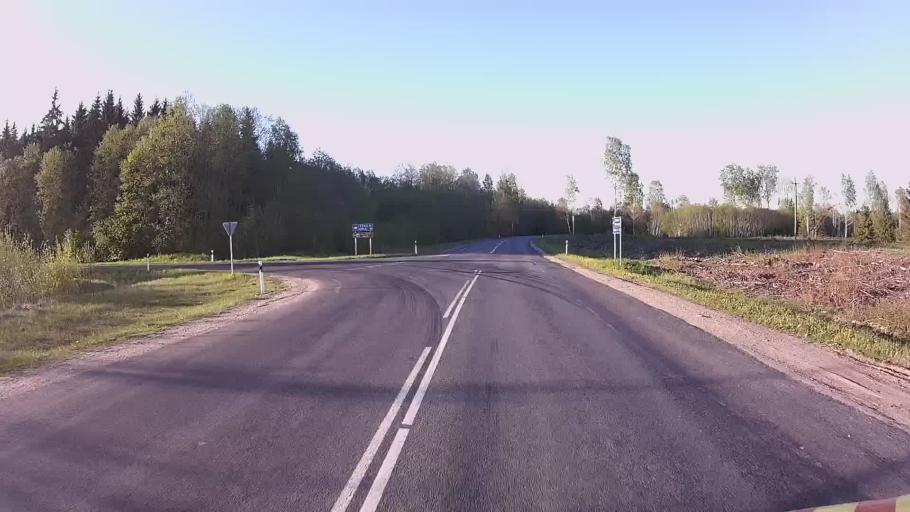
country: EE
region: Viljandimaa
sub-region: Viiratsi vald
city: Viiratsi
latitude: 58.4624
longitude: 25.7512
